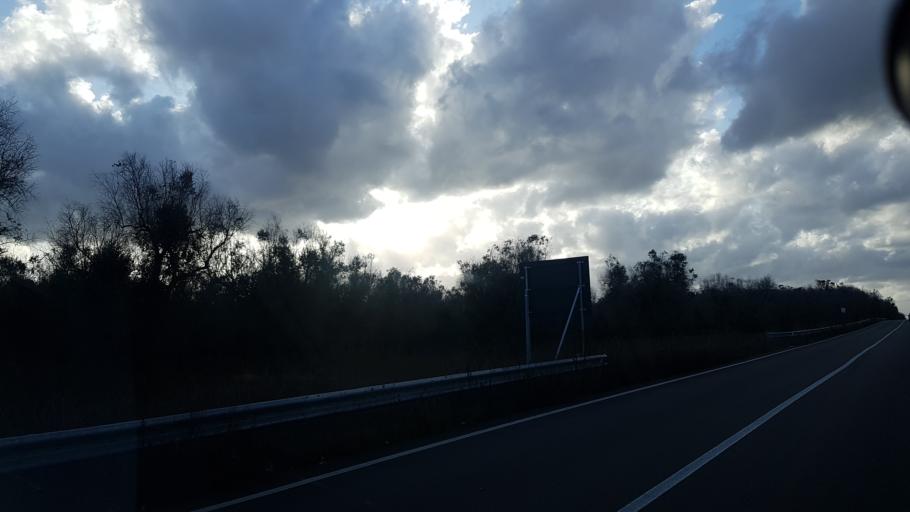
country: IT
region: Apulia
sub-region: Provincia di Brindisi
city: Torchiarolo
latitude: 40.4869
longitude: 18.0356
